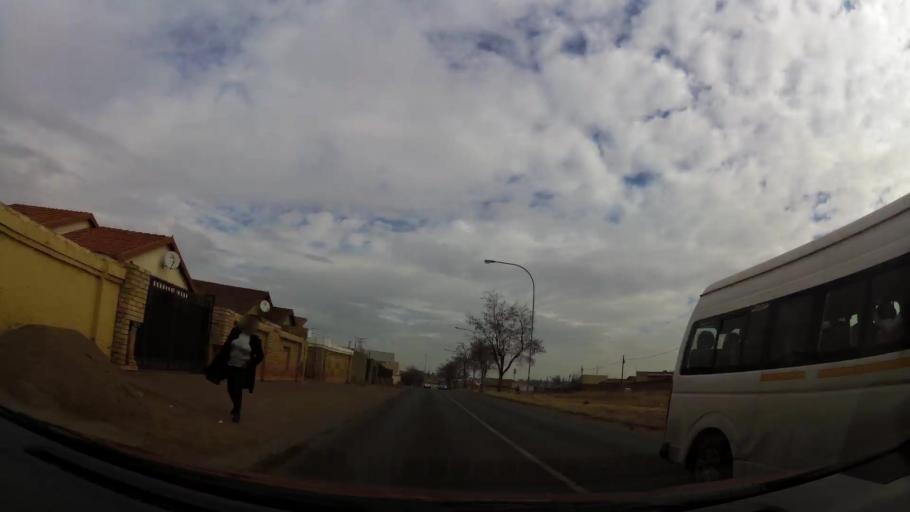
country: ZA
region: Gauteng
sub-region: City of Johannesburg Metropolitan Municipality
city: Soweto
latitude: -26.2724
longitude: 27.8413
